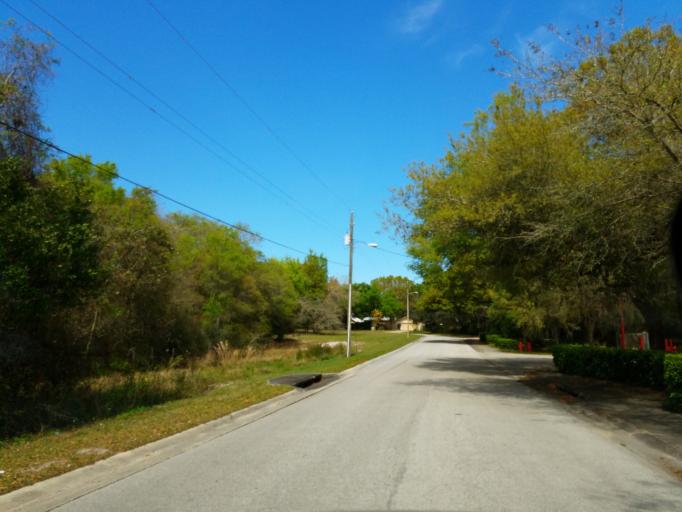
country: US
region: Florida
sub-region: Hillsborough County
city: Thonotosassa
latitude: 28.0645
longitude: -82.3069
